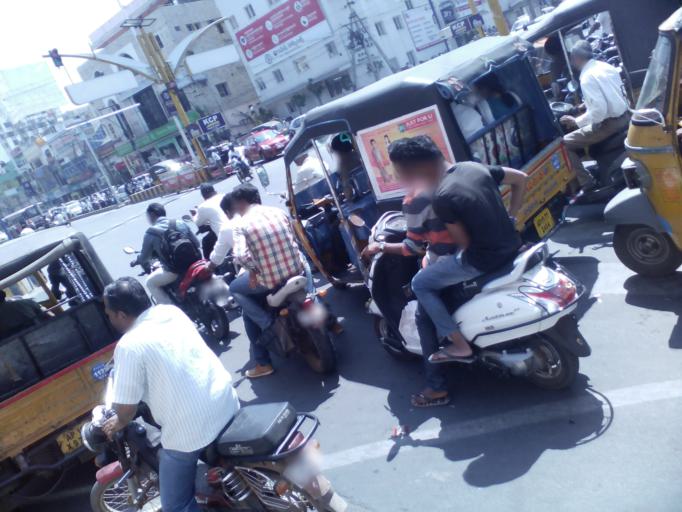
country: IN
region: Andhra Pradesh
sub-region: Krishna
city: Vijayawada
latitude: 16.5034
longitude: 80.6385
